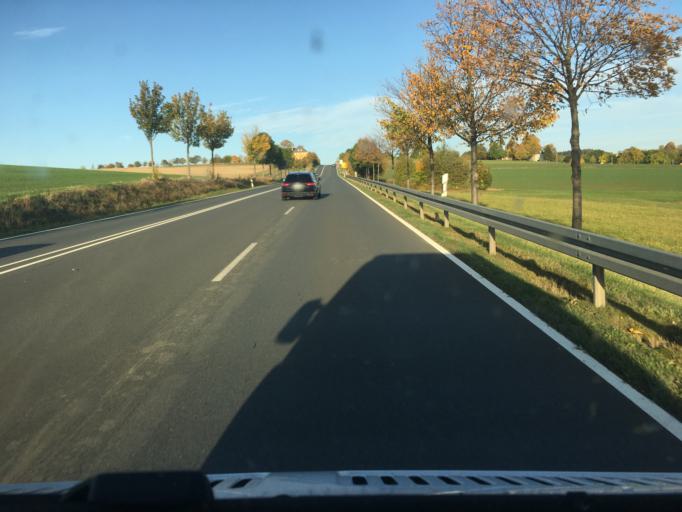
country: DE
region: Saxony
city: Schneeberg
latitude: 50.6000
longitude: 12.6220
